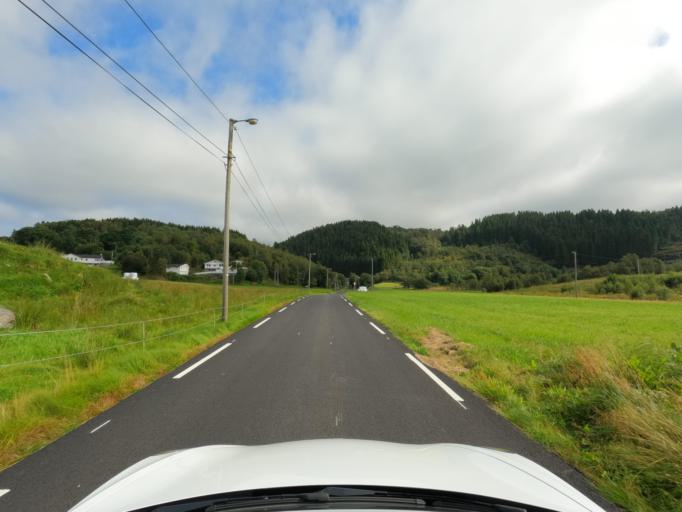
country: NO
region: Hordaland
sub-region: Os
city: Syfteland
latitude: 60.3063
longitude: 5.4099
